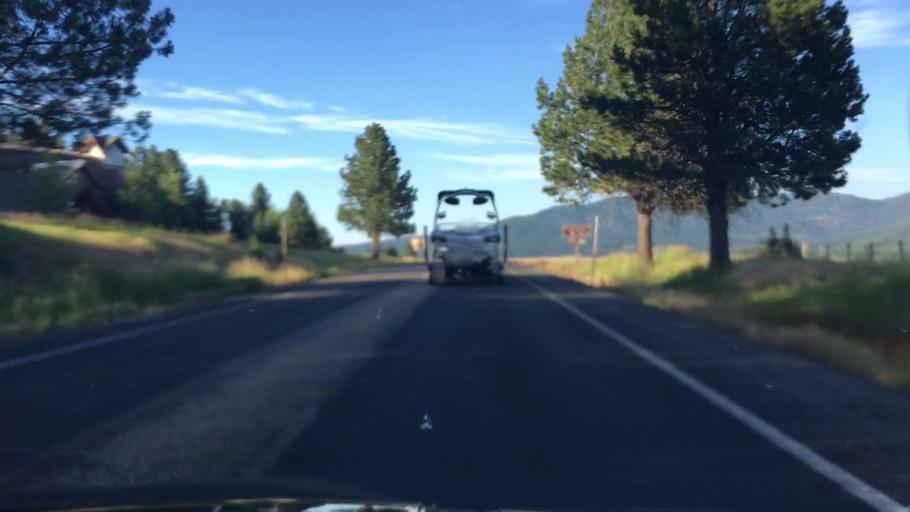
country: US
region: Idaho
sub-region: Valley County
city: Cascade
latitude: 44.5290
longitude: -116.0403
